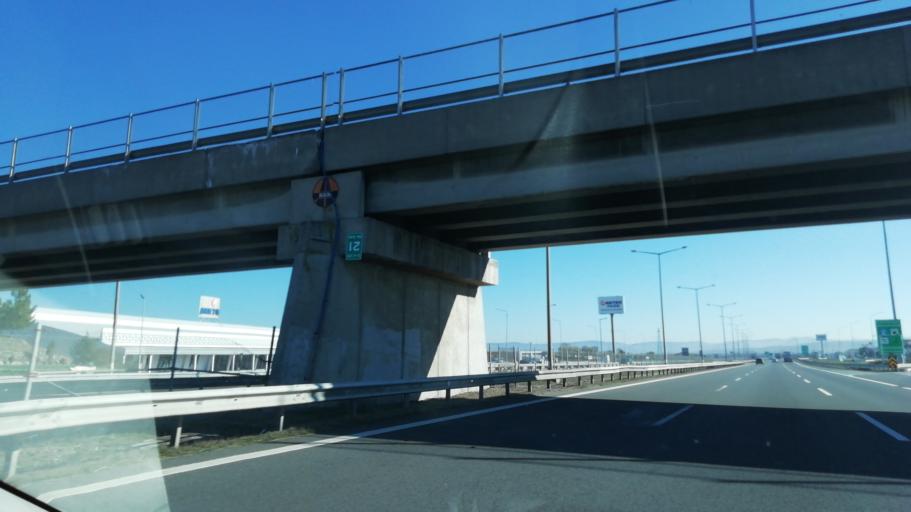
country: TR
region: Bolu
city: Dortdivan
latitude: 40.7509
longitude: 32.0805
